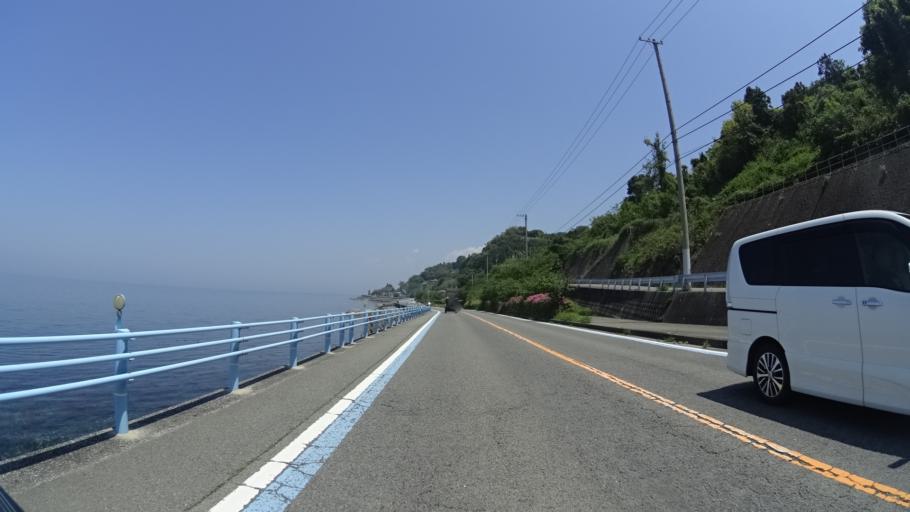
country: JP
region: Ehime
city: Iyo
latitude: 33.6657
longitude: 132.6060
